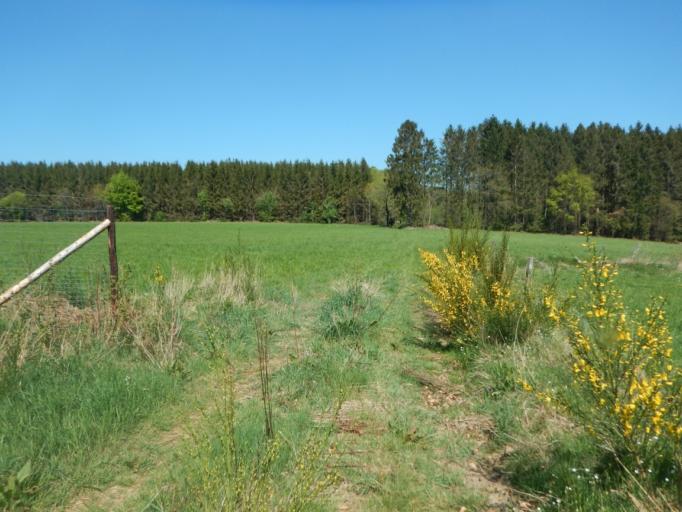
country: LU
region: Diekirch
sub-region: Canton de Clervaux
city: Weiswampach
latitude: 50.1533
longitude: 6.0403
